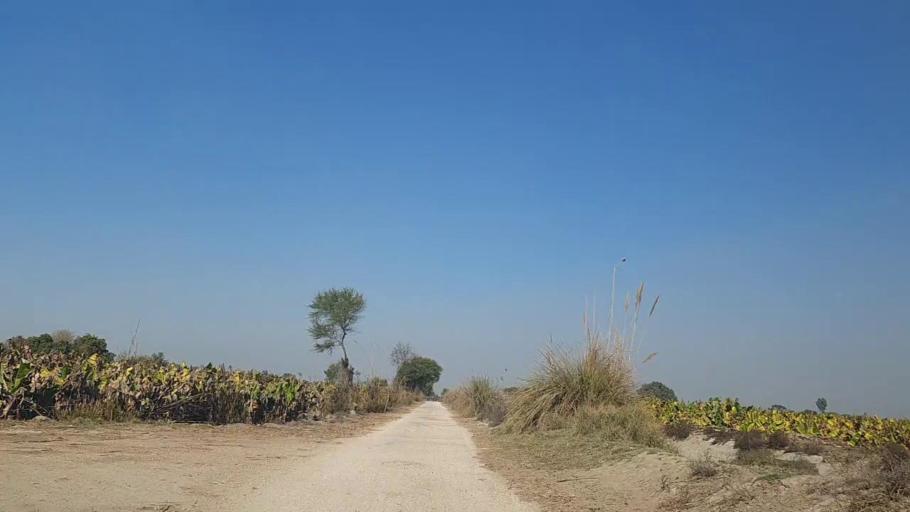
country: PK
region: Sindh
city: Sakrand
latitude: 26.2604
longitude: 68.2209
